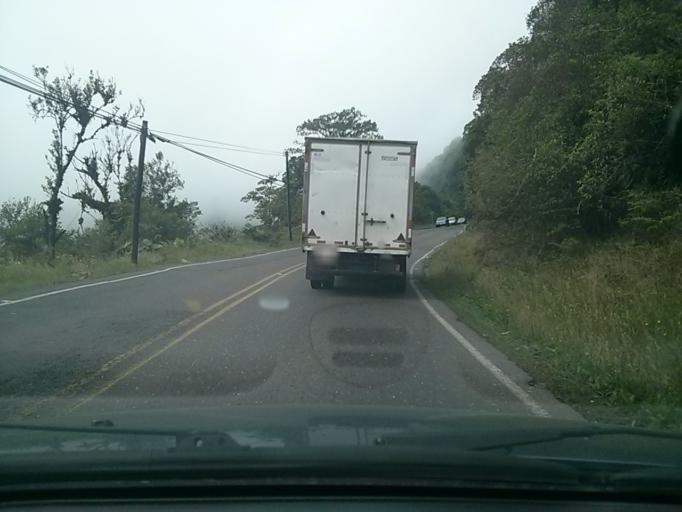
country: CR
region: San Jose
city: San Marcos
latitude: 9.7388
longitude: -83.9509
